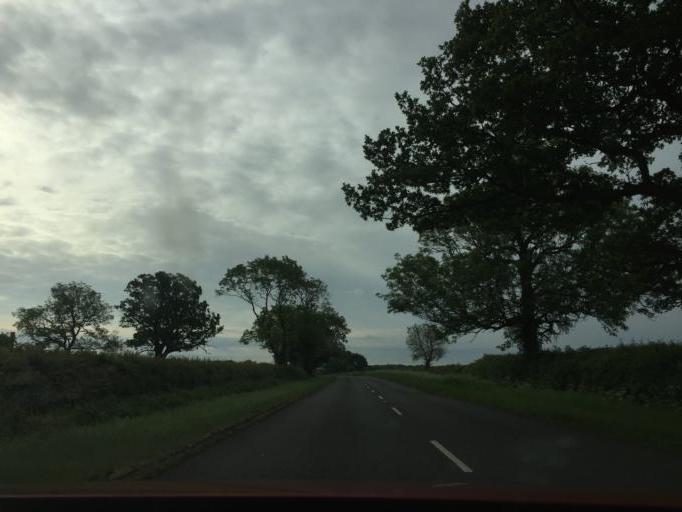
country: GB
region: England
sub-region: Leicestershire
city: Hinckley
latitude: 52.4848
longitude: -1.3409
